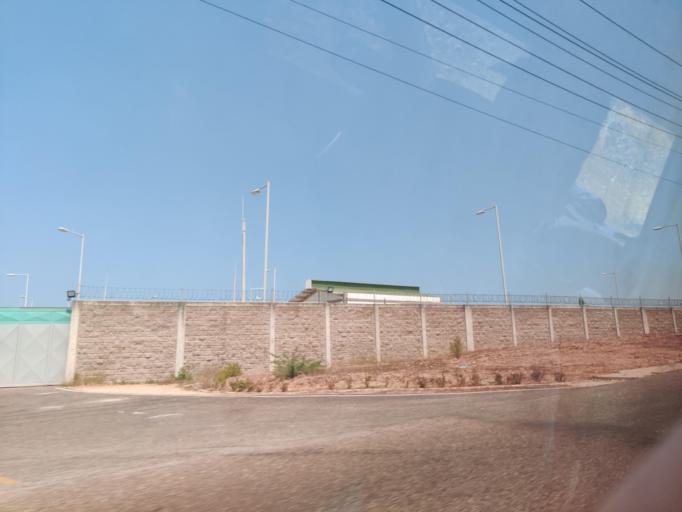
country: CO
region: Bolivar
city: Turbana
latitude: 10.2709
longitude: -75.5510
